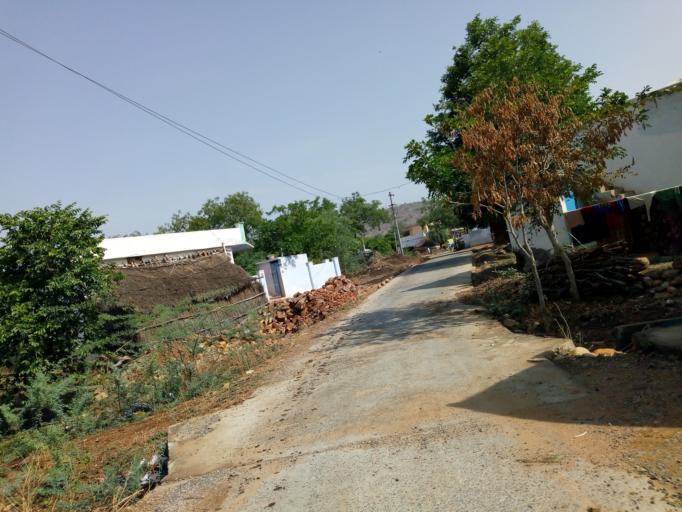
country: IN
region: Andhra Pradesh
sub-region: Prakasam
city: Cumbum
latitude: 15.7157
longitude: 79.0778
